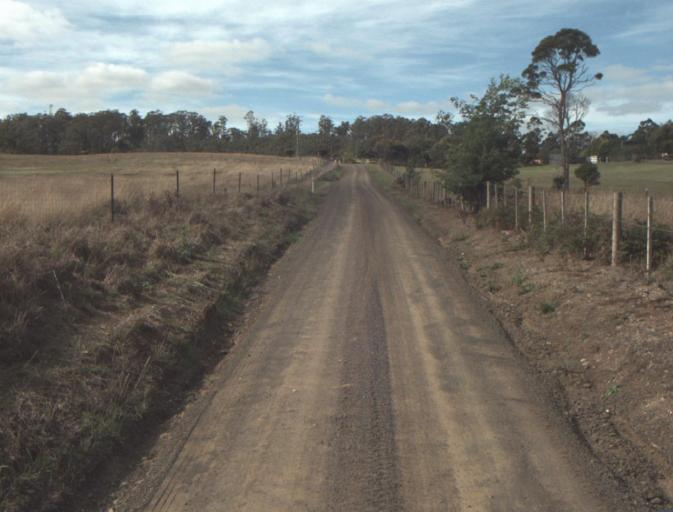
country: AU
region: Tasmania
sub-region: Launceston
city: Mayfield
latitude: -41.1916
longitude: 147.1890
